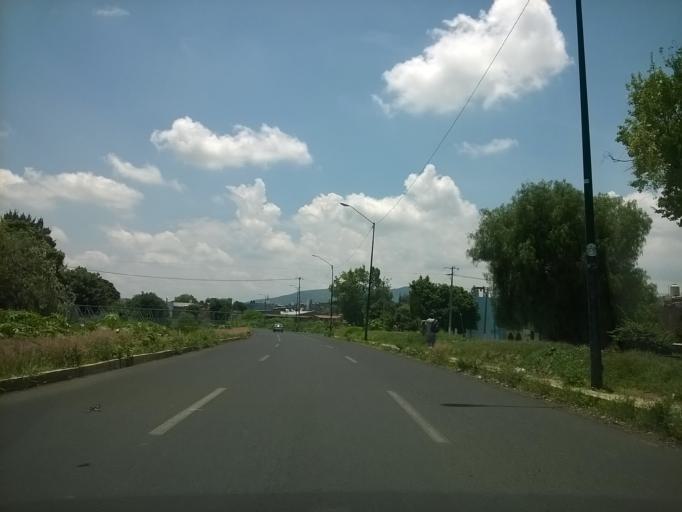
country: MX
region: Michoacan
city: Morelia
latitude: 19.7120
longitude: -101.1920
